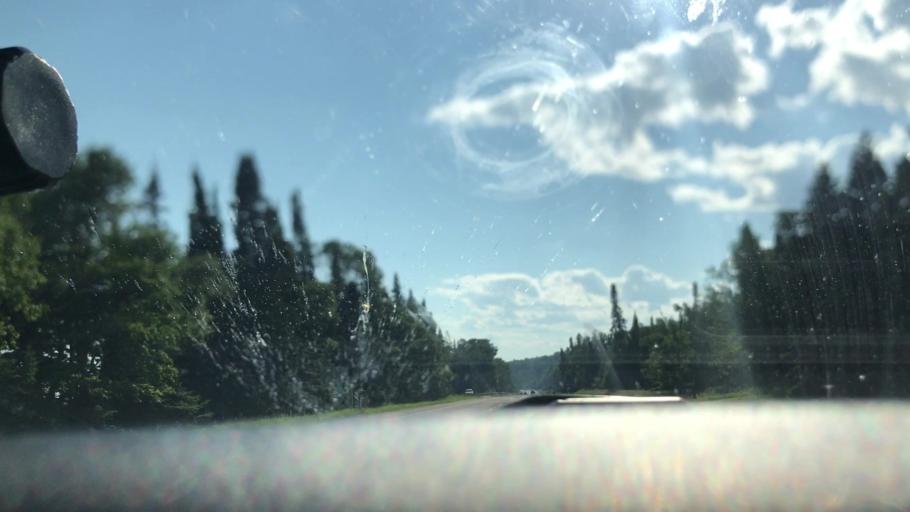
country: US
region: Minnesota
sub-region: Cook County
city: Grand Marais
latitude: 47.7945
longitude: -90.1515
